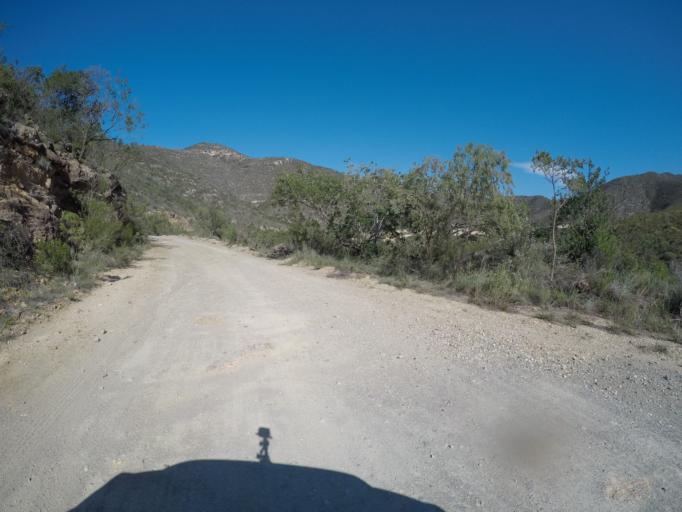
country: ZA
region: Eastern Cape
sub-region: Cacadu District Municipality
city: Kareedouw
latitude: -33.6525
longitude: 24.5029
